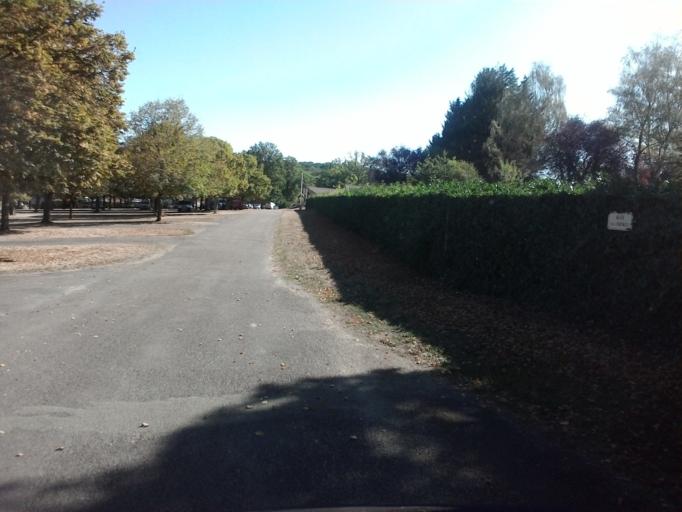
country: FR
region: Bourgogne
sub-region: Departement de la Cote-d'Or
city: Semur-en-Auxois
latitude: 47.4685
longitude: 4.3546
